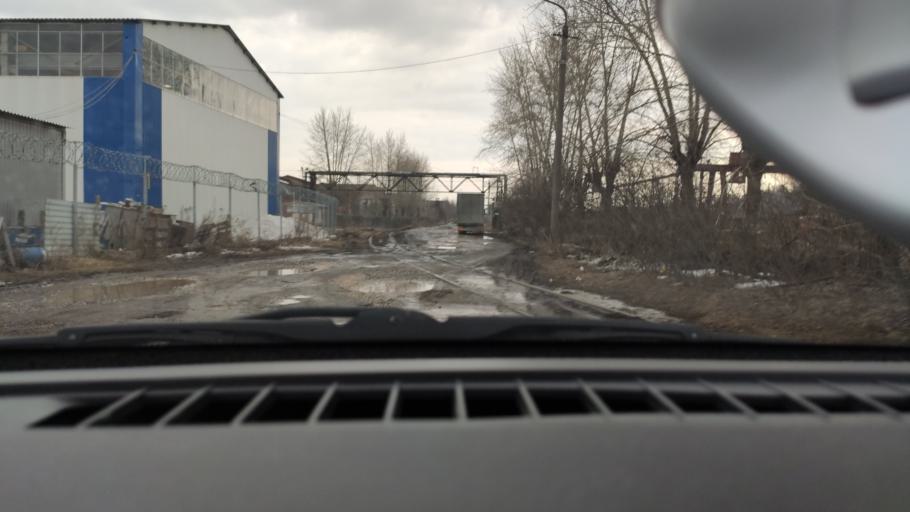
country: RU
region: Perm
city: Perm
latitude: 58.0455
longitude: 56.3143
